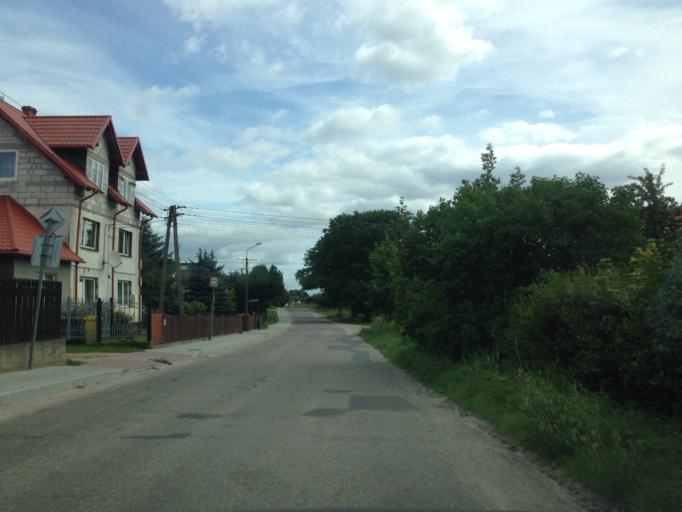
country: PL
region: Pomeranian Voivodeship
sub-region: Powiat koscierski
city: Lipusz
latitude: 54.0922
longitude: 17.7747
